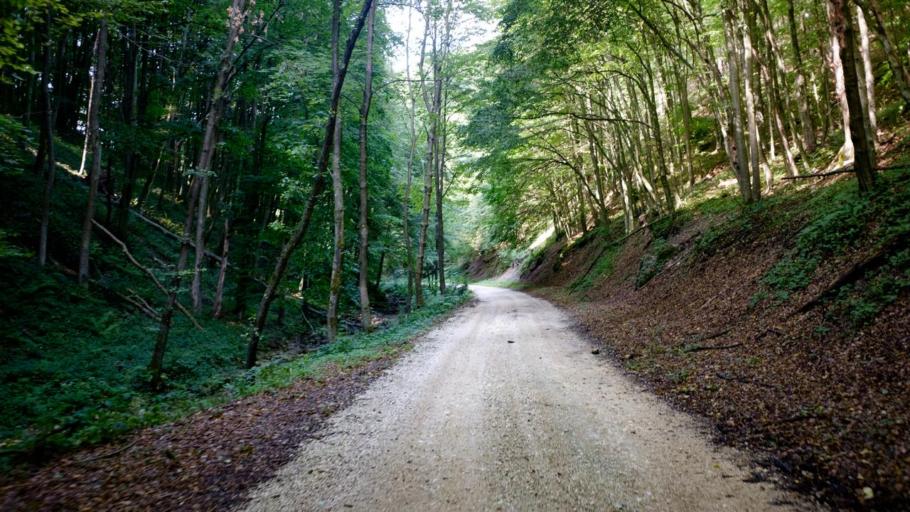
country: HU
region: Gyor-Moson-Sopron
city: Bakonyszentlaszlo
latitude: 47.3379
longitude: 17.8146
